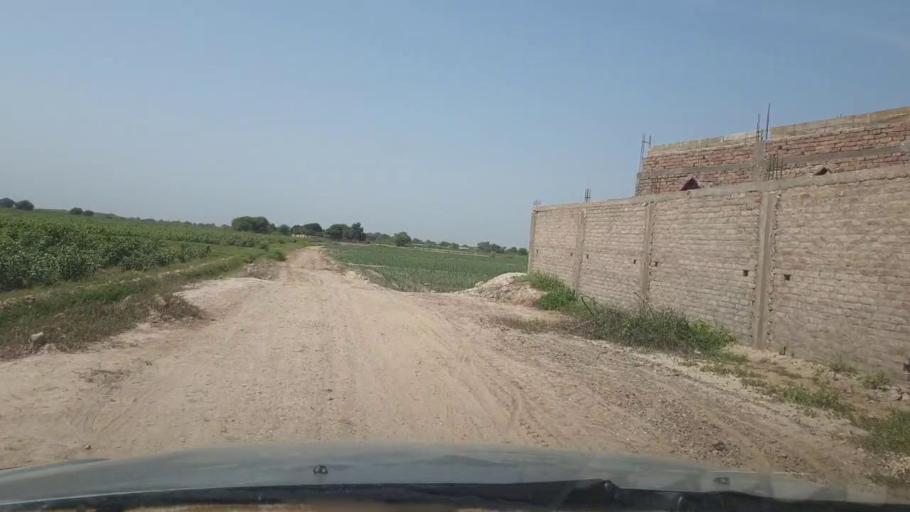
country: PK
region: Sindh
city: Chambar
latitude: 25.2594
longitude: 68.7540
